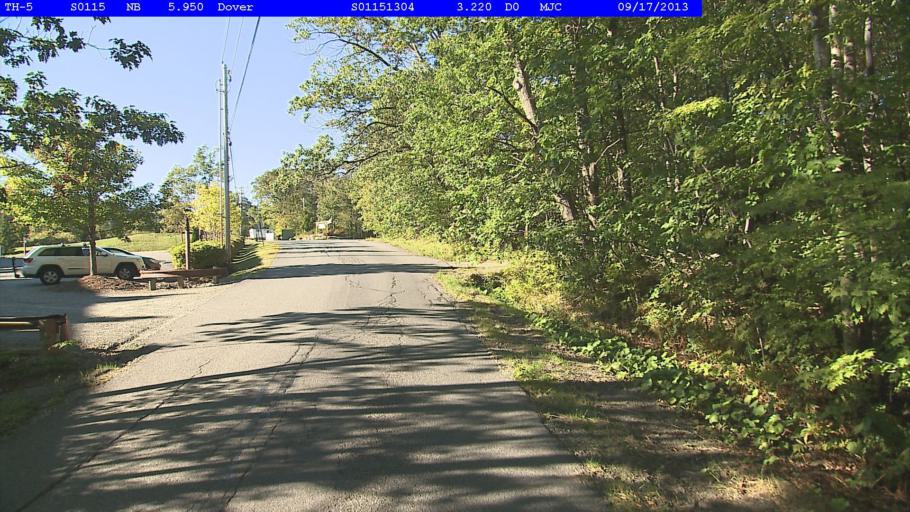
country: US
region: Vermont
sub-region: Windham County
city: Dover
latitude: 42.9704
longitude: -72.8902
